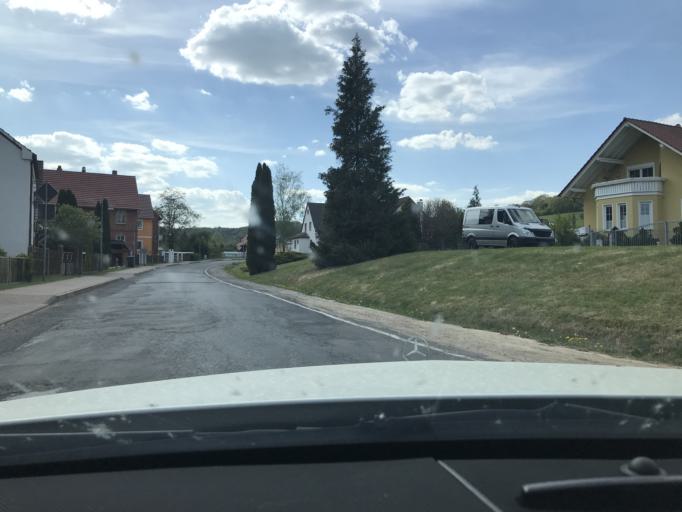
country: DE
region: Hesse
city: Wanfried
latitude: 51.1369
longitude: 10.1643
